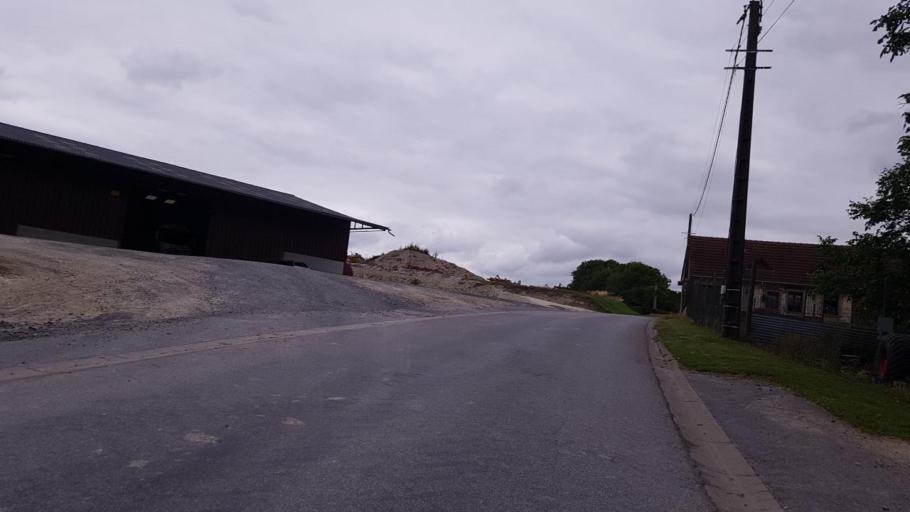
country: FR
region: Picardie
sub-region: Departement de l'Aisne
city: Guise
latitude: 49.8853
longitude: 3.5601
